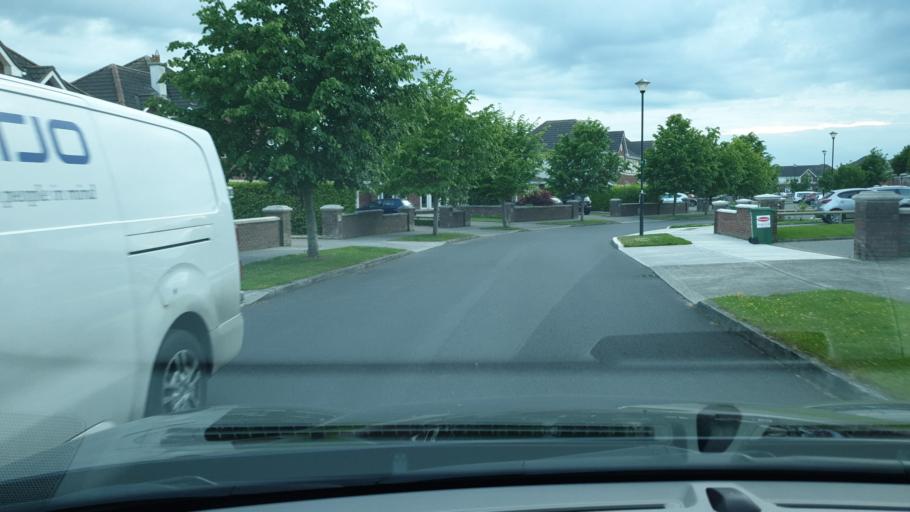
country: IE
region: Leinster
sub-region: An Mhi
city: Ashbourne
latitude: 53.5131
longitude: -6.3862
